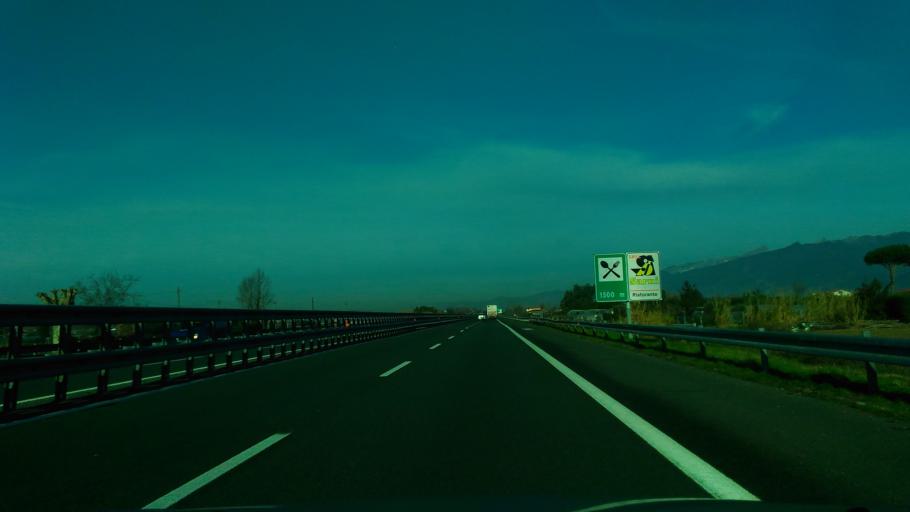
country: IT
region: Tuscany
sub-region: Provincia di Lucca
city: Camaiore
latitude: 43.9158
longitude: 10.2351
